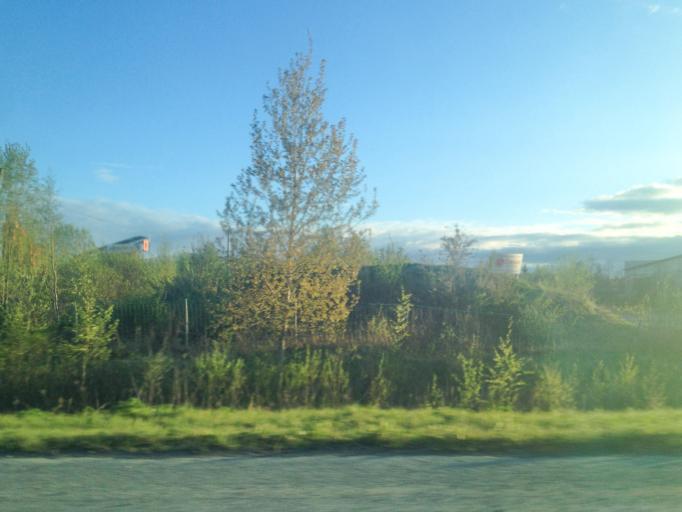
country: FI
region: Haeme
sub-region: Haemeenlinna
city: Haemeenlinna
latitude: 61.0173
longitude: 24.4092
